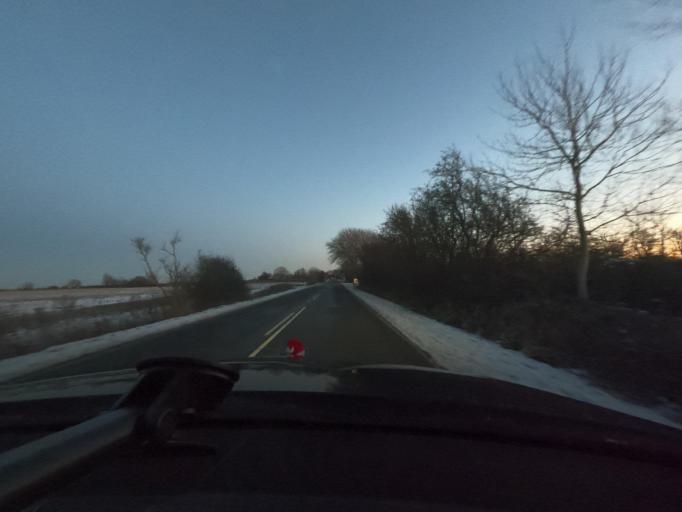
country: DK
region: South Denmark
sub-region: Sonderborg Kommune
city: Horuphav
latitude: 54.8594
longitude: 9.9733
